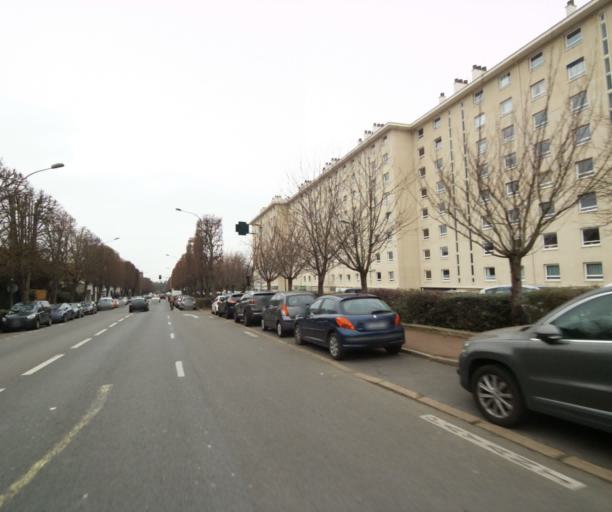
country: FR
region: Ile-de-France
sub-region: Departement des Hauts-de-Seine
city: Saint-Cloud
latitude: 48.8530
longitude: 2.2126
